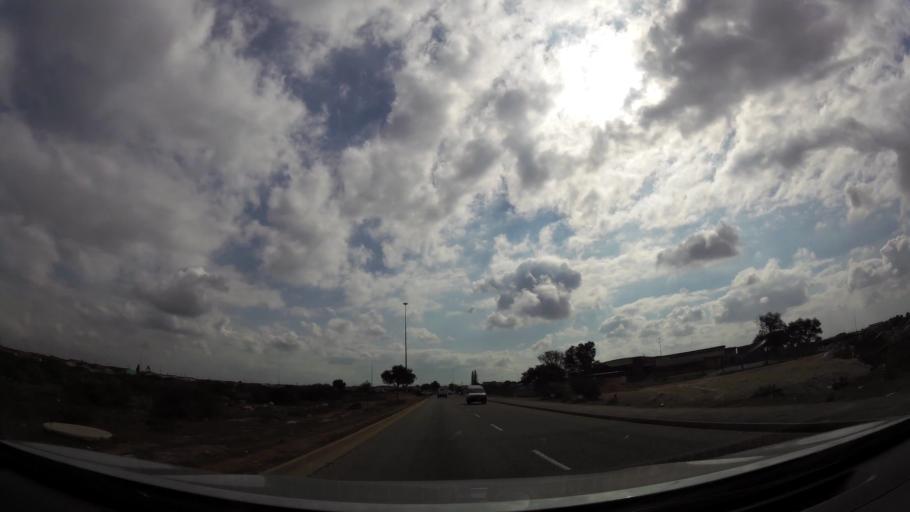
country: ZA
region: Eastern Cape
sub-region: Nelson Mandela Bay Metropolitan Municipality
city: Port Elizabeth
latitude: -33.8147
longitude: 25.5920
